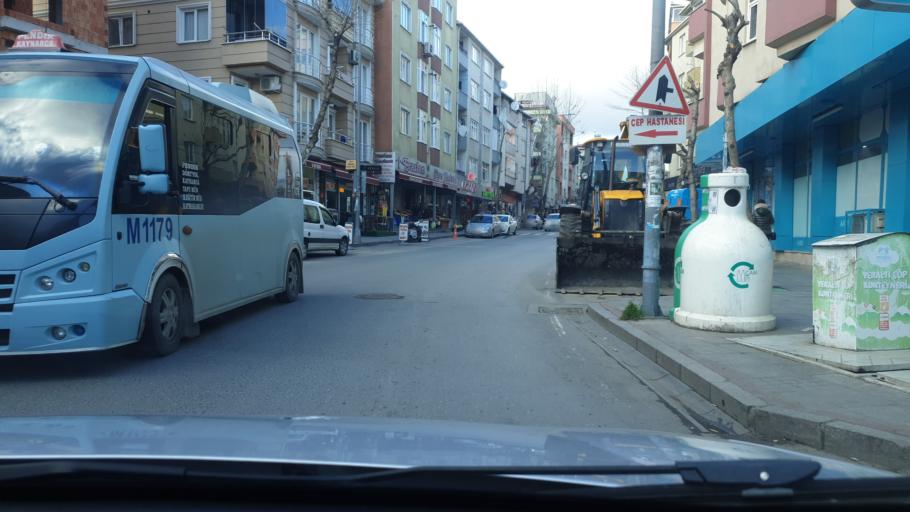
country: TR
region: Istanbul
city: Pendik
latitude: 40.8748
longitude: 29.2725
